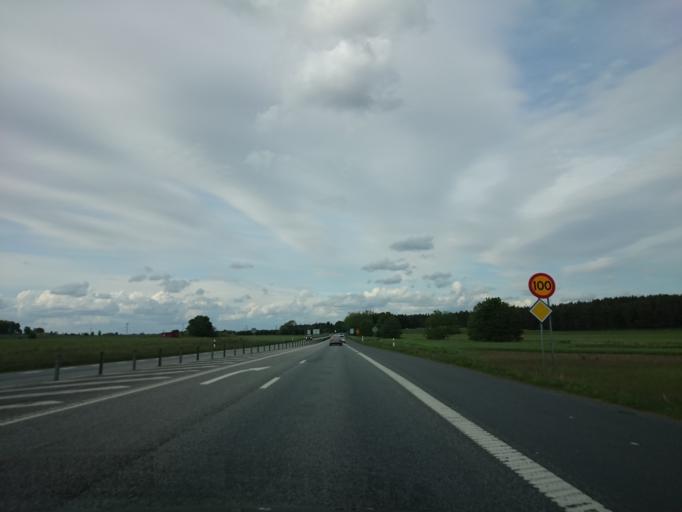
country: SE
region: Skane
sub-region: Kristianstads Kommun
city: Norra Asum
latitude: 55.9581
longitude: 14.0672
